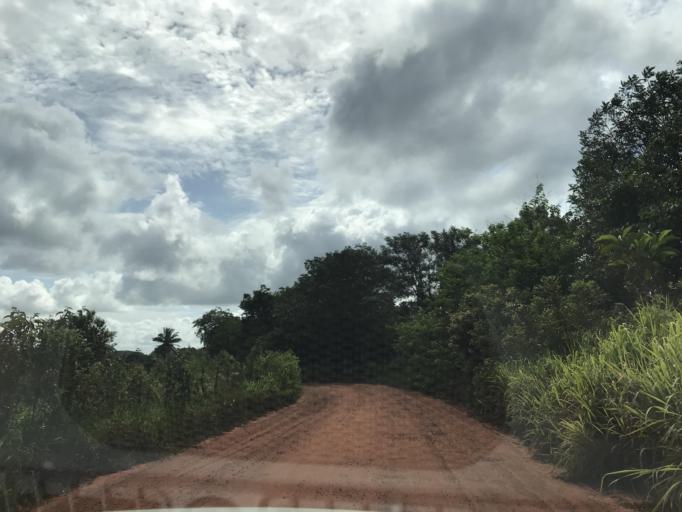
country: BR
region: Bahia
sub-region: Entre Rios
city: Entre Rios
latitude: -12.1710
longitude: -38.1495
